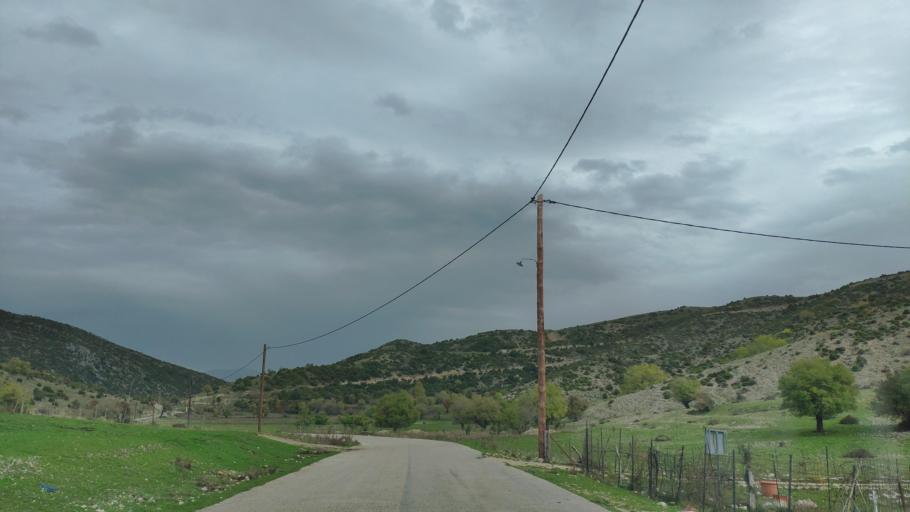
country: GR
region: Epirus
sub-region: Nomos Thesprotias
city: Paramythia
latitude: 39.4468
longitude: 20.6437
